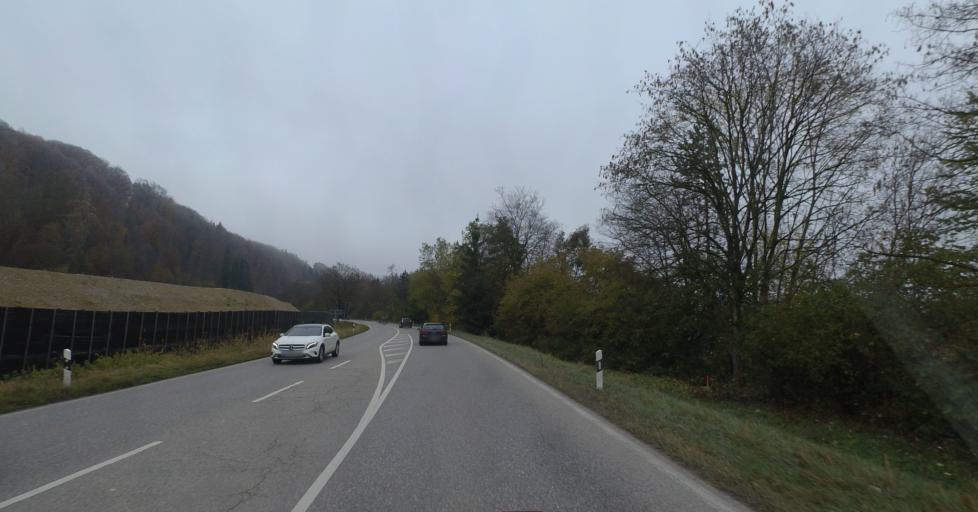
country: DE
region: Bavaria
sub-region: Upper Bavaria
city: Trostberg an der Alz
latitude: 48.0081
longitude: 12.5327
